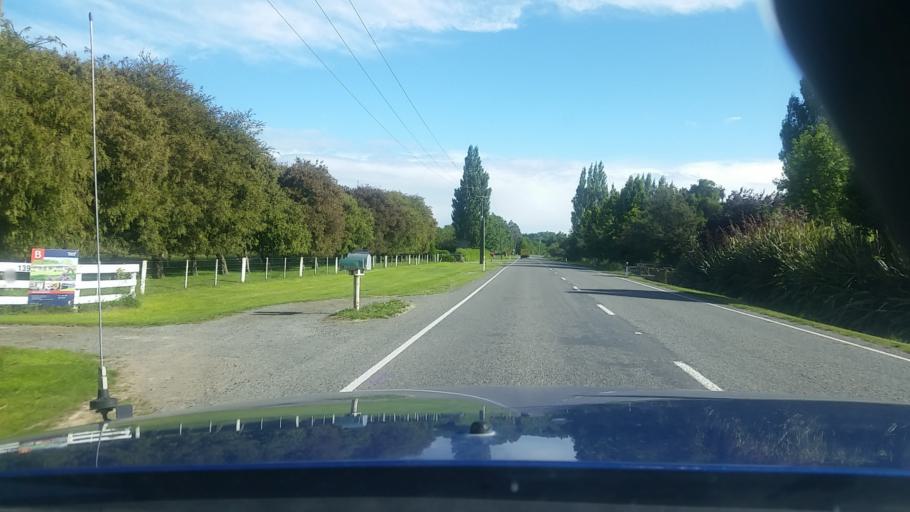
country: NZ
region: Canterbury
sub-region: Ashburton District
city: Ashburton
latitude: -43.8712
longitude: 171.7274
